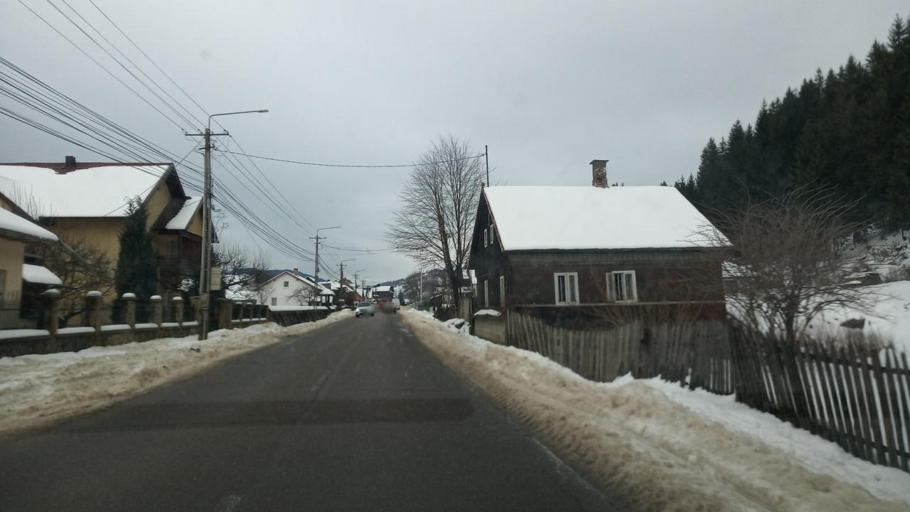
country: RO
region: Suceava
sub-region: Comuna Manastirea Humorului
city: Manastirea Humorului
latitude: 47.5862
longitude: 25.8701
